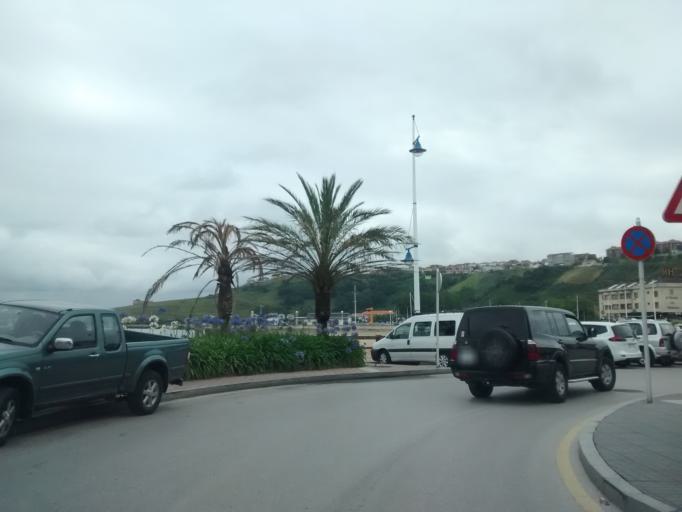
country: ES
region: Cantabria
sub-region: Provincia de Cantabria
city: Suances
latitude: 43.4328
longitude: -4.0358
